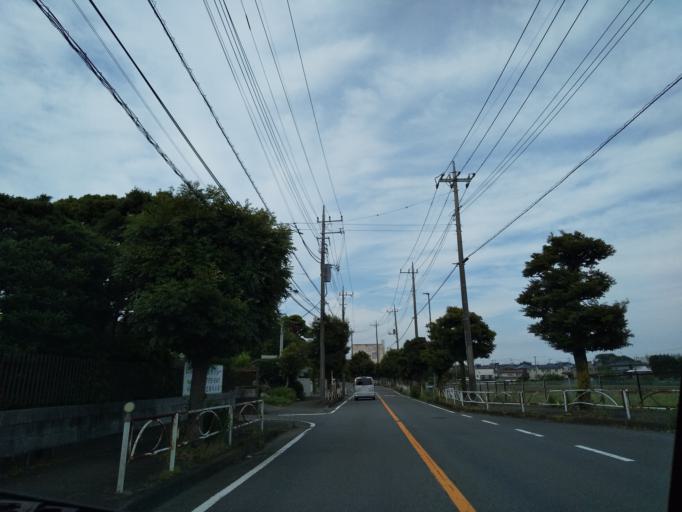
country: JP
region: Kanagawa
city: Atsugi
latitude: 35.4834
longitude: 139.3218
